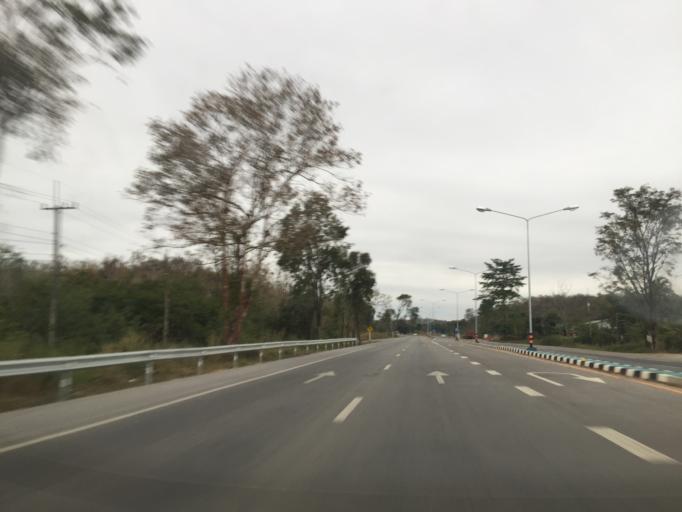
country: TH
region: Loei
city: Erawan
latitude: 17.3141
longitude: 101.9084
